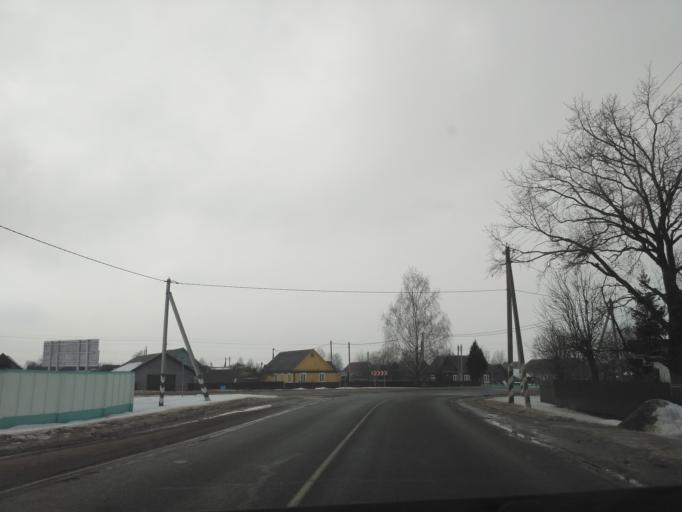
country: BY
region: Minsk
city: Horad Smalyavichy
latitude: 54.0258
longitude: 28.0656
